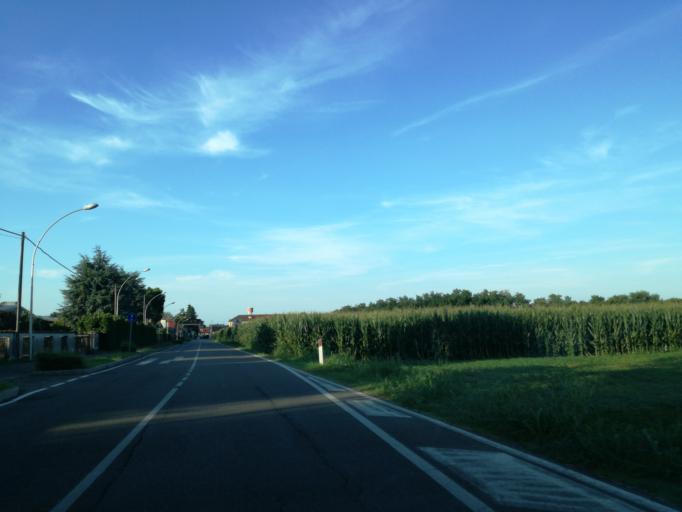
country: IT
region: Lombardy
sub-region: Provincia di Monza e Brianza
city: Sulbiate
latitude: 45.6454
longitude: 9.4288
